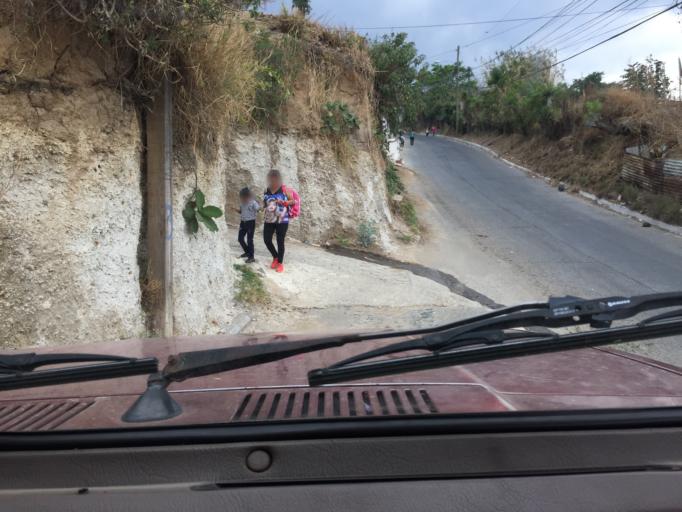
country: GT
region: Guatemala
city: Amatitlan
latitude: 14.4956
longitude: -90.6436
